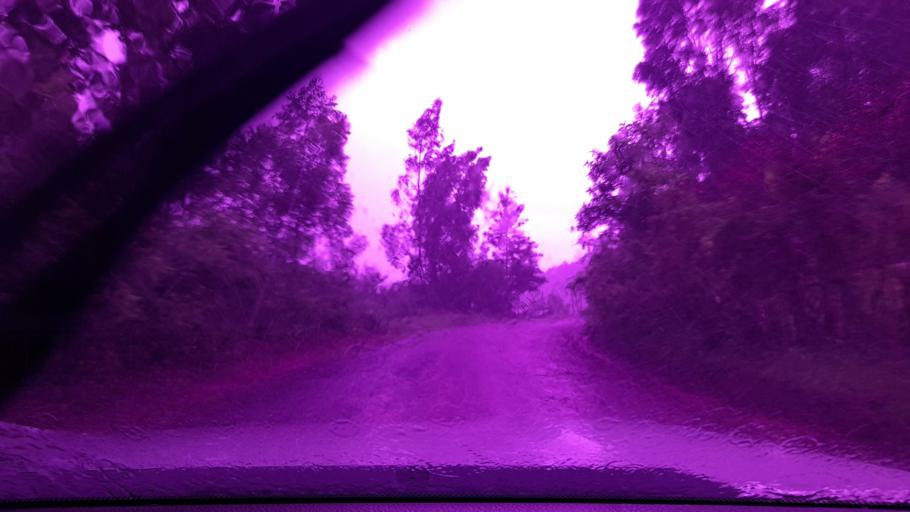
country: ET
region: Oromiya
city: Metu
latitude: 8.3680
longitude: 35.5948
